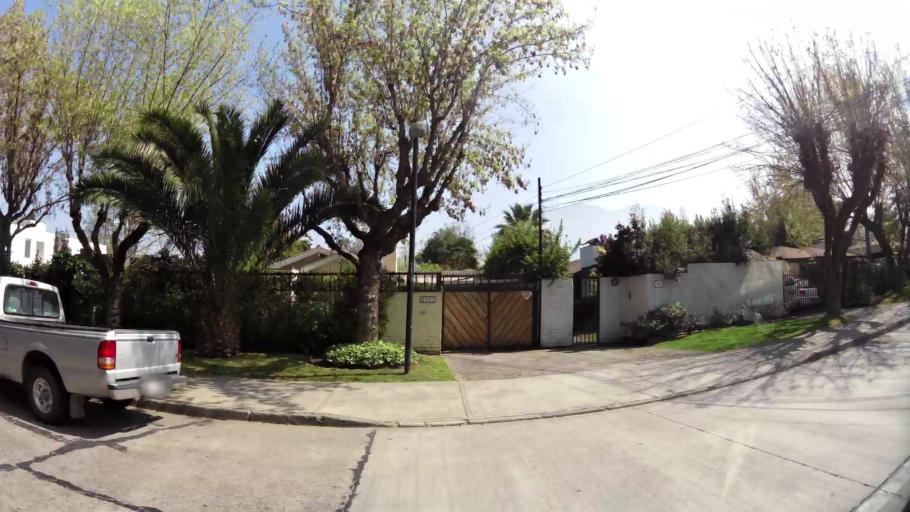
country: CL
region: Santiago Metropolitan
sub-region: Provincia de Santiago
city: Villa Presidente Frei, Nunoa, Santiago, Chile
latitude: -33.3863
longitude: -70.5795
